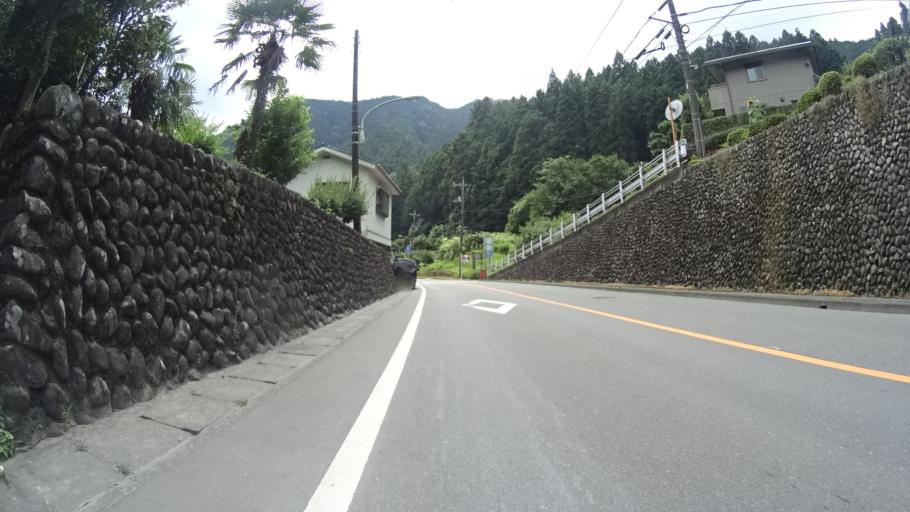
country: JP
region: Tokyo
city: Ome
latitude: 35.8074
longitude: 139.1682
